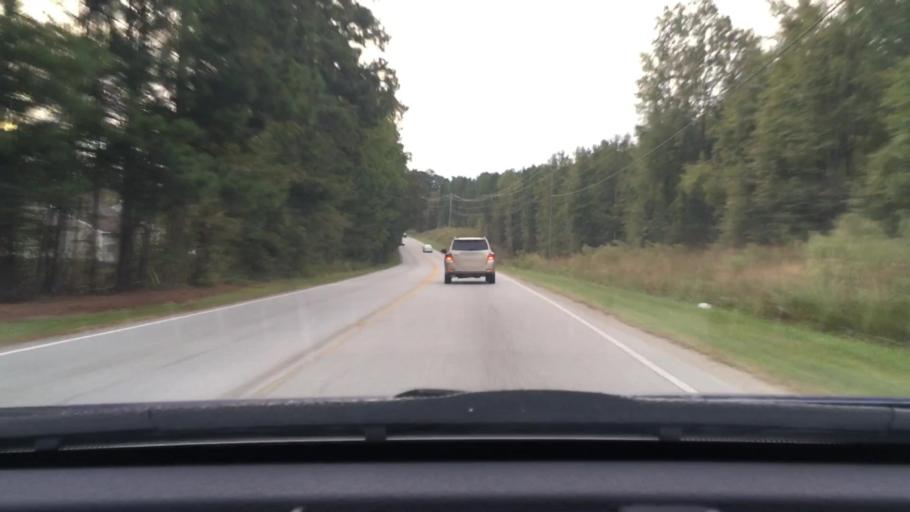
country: US
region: South Carolina
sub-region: Lexington County
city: Irmo
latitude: 34.0903
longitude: -81.1511
